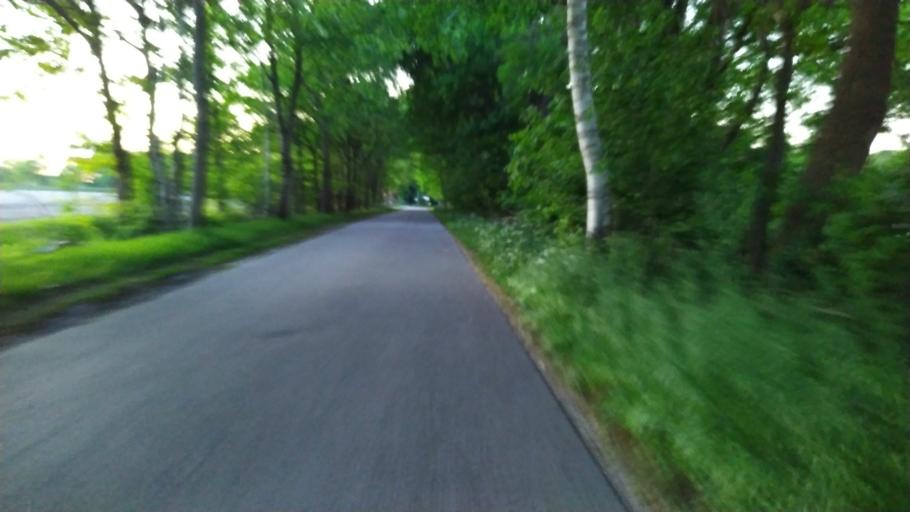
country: DE
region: Lower Saxony
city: Bargstedt
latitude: 53.4808
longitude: 9.4664
